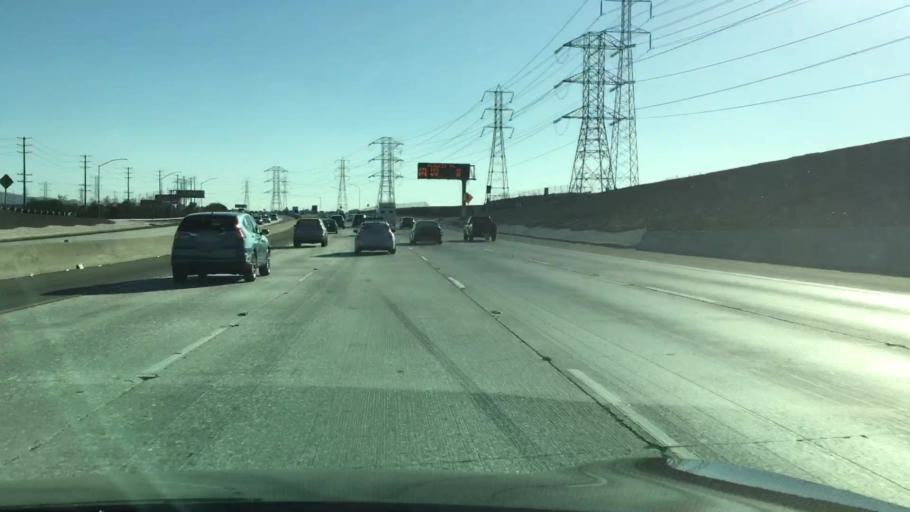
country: US
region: California
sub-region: Los Angeles County
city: Mayflower Village
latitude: 34.0913
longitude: -117.9925
